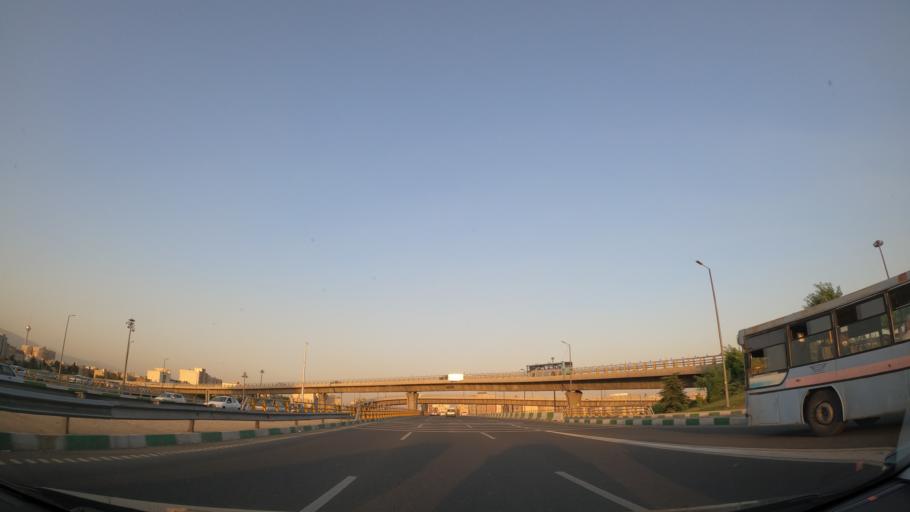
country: IR
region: Tehran
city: Tehran
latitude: 35.7126
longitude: 51.3346
